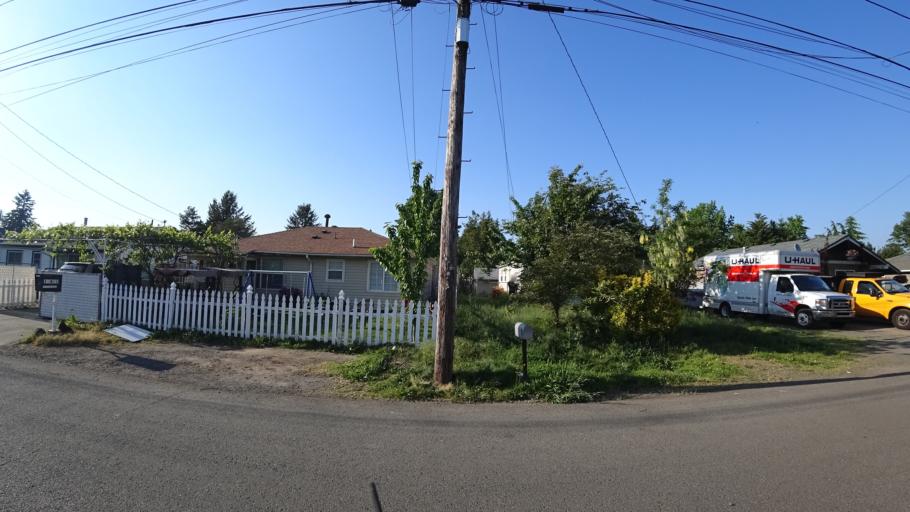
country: US
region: Oregon
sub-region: Multnomah County
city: Gresham
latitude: 45.5123
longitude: -122.4939
